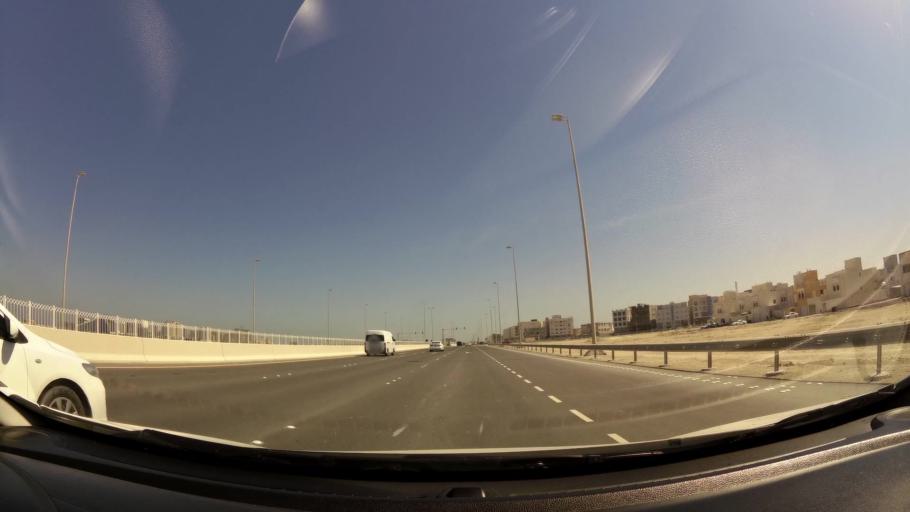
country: BH
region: Muharraq
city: Al Hadd
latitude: 26.2849
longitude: 50.6434
